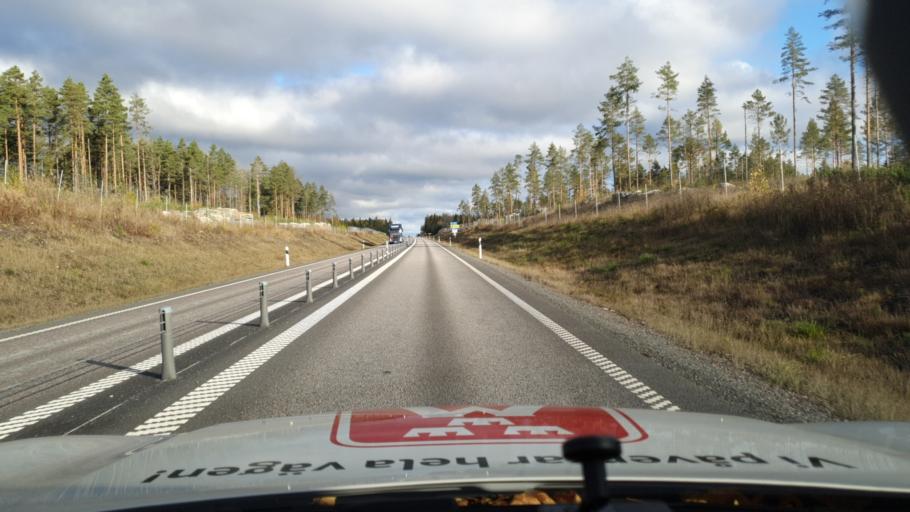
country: SE
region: Uppsala
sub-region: Heby Kommun
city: Tarnsjo
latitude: 60.0870
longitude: 16.9173
